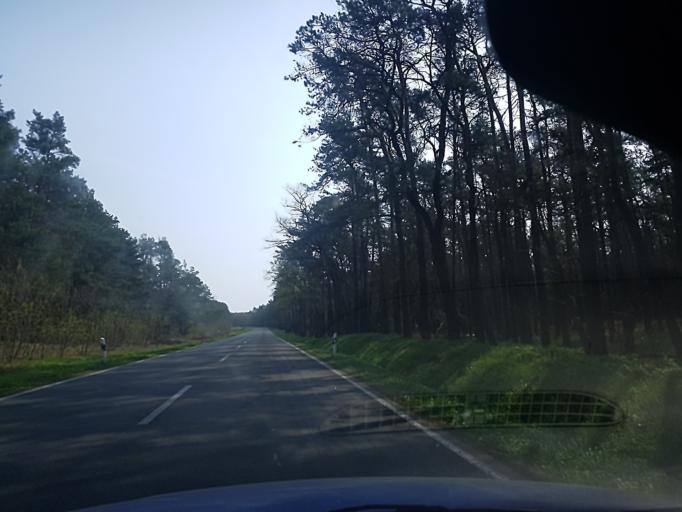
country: DE
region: Saxony
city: Beilrode
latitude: 51.5901
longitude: 13.0956
